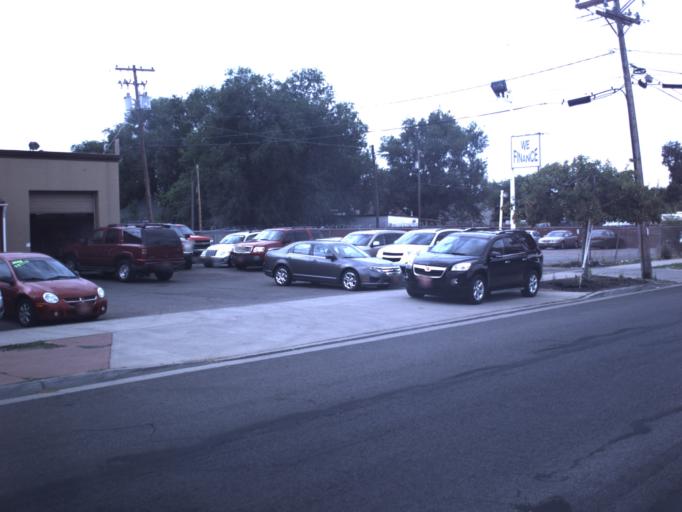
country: US
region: Utah
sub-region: Weber County
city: Ogden
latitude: 41.2103
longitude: -111.9711
